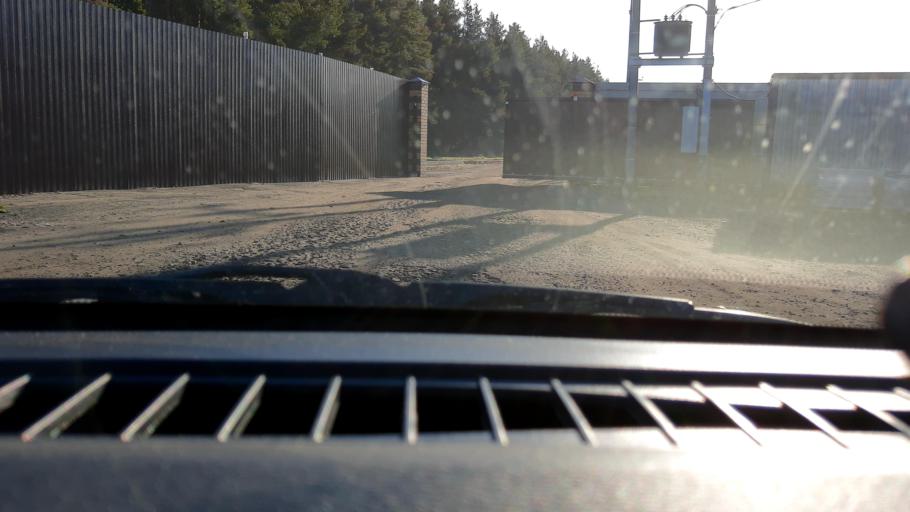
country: RU
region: Nizjnij Novgorod
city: Gorbatovka
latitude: 56.3044
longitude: 43.7382
